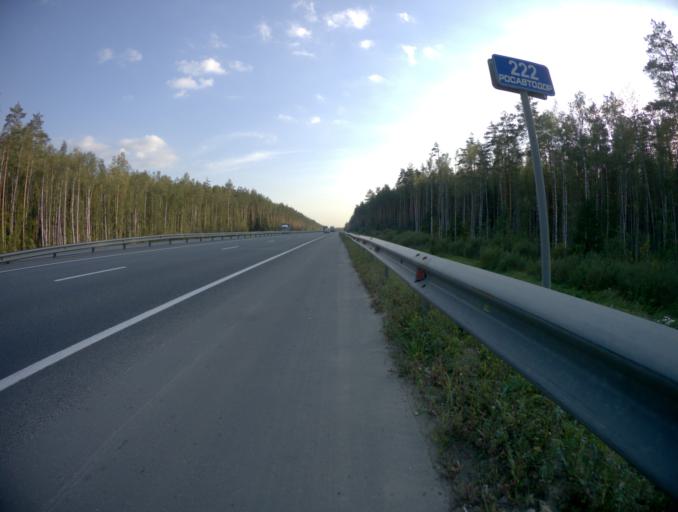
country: RU
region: Vladimir
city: Kameshkovo
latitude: 56.1890
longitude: 40.9495
